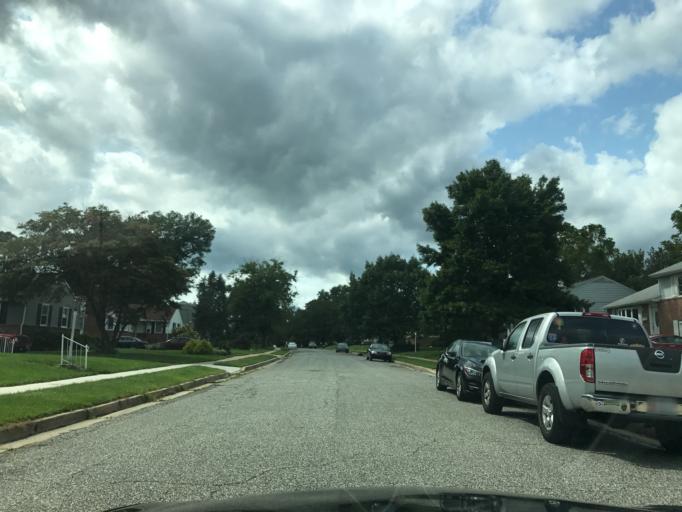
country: US
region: Maryland
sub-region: Baltimore County
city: Mays Chapel
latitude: 39.4200
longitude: -76.6445
